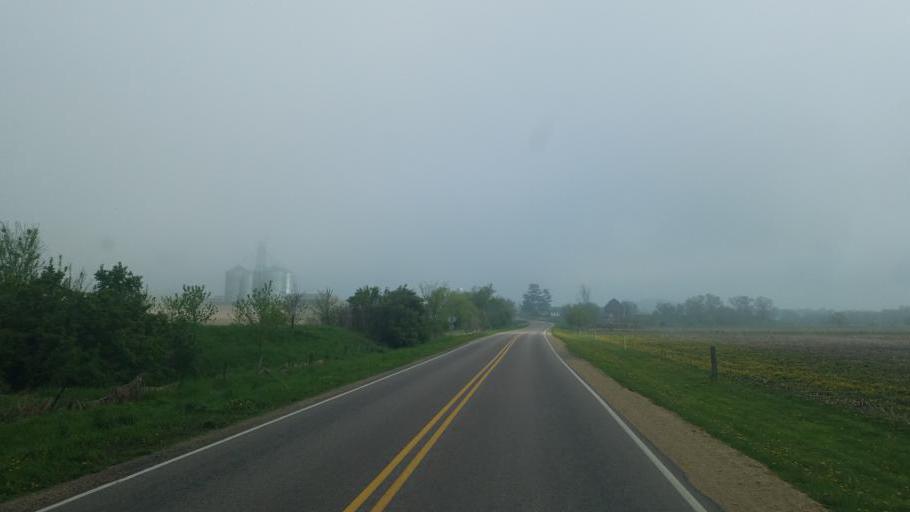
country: US
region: Wisconsin
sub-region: Vernon County
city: Hillsboro
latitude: 43.6355
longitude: -90.3526
